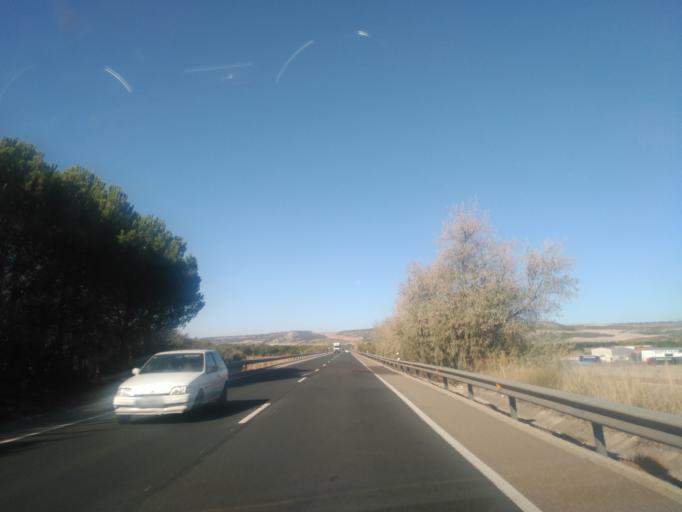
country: ES
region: Castille and Leon
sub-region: Provincia de Valladolid
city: Quintanilla de Onesimo
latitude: 41.6200
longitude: -4.3709
